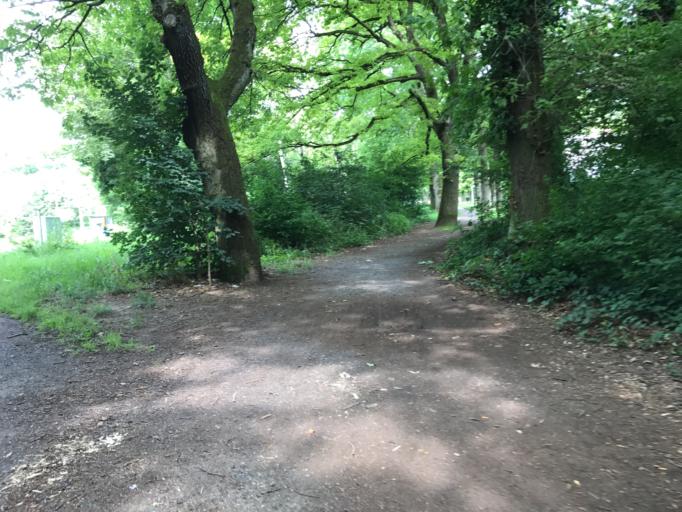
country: DE
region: Hesse
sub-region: Regierungsbezirk Darmstadt
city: Walluf
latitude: 50.0701
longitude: 8.1788
